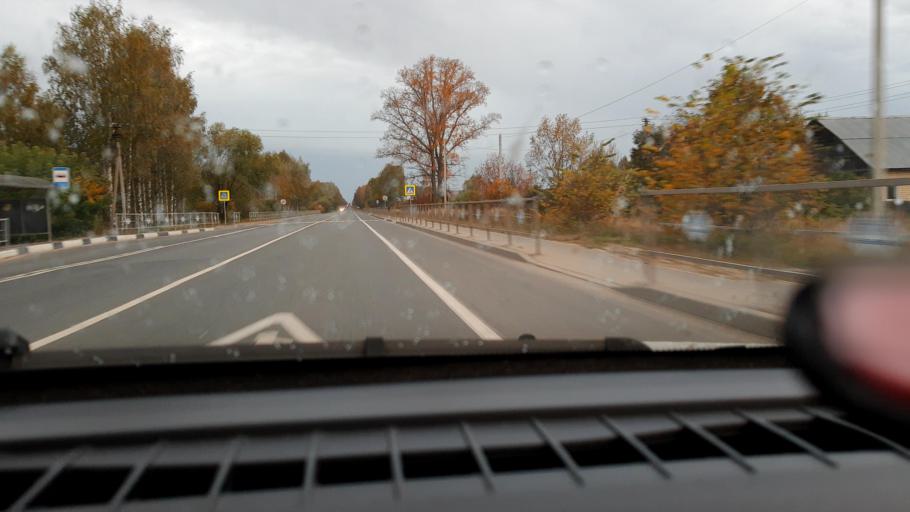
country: RU
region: Vladimir
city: Orgtrud
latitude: 56.2032
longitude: 40.7561
